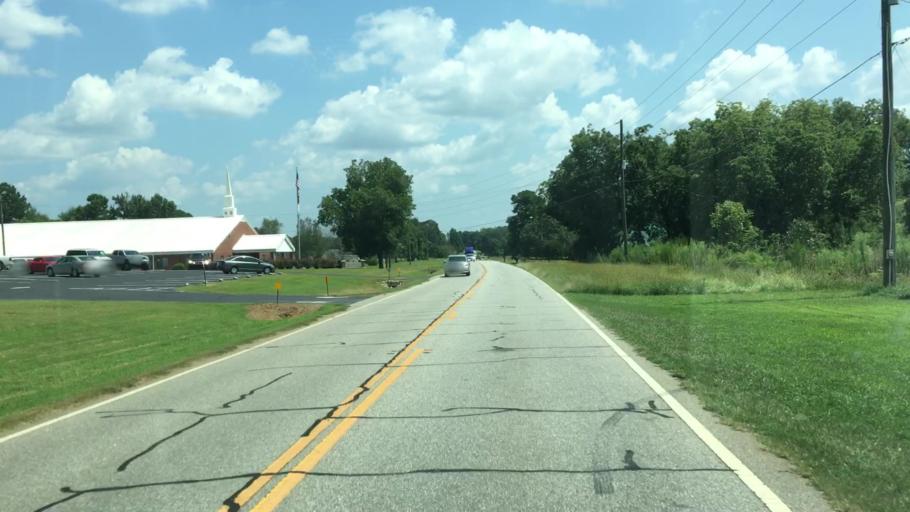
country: US
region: Georgia
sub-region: Barrow County
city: Statham
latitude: 33.9422
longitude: -83.6424
